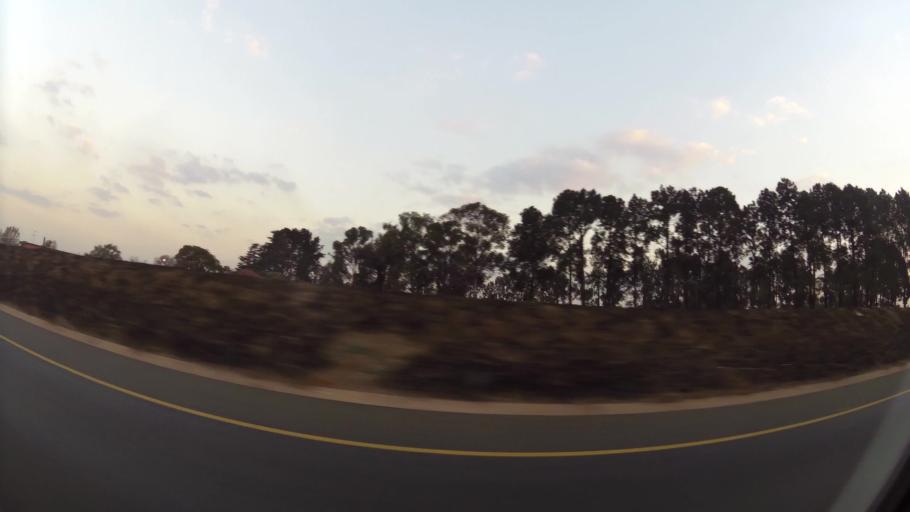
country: ZA
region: Gauteng
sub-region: Ekurhuleni Metropolitan Municipality
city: Springs
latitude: -26.2763
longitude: 28.3863
